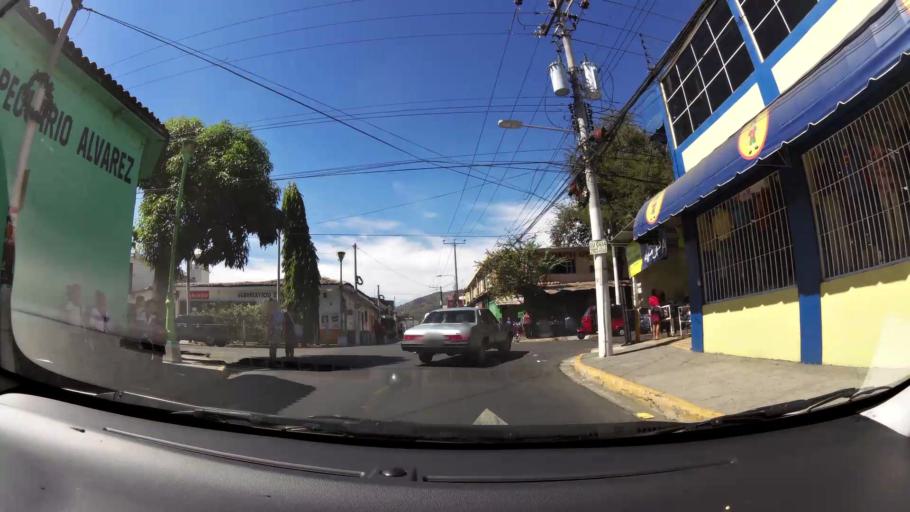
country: SV
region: San Salvador
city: Apopa
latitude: 13.8023
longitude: -89.1777
